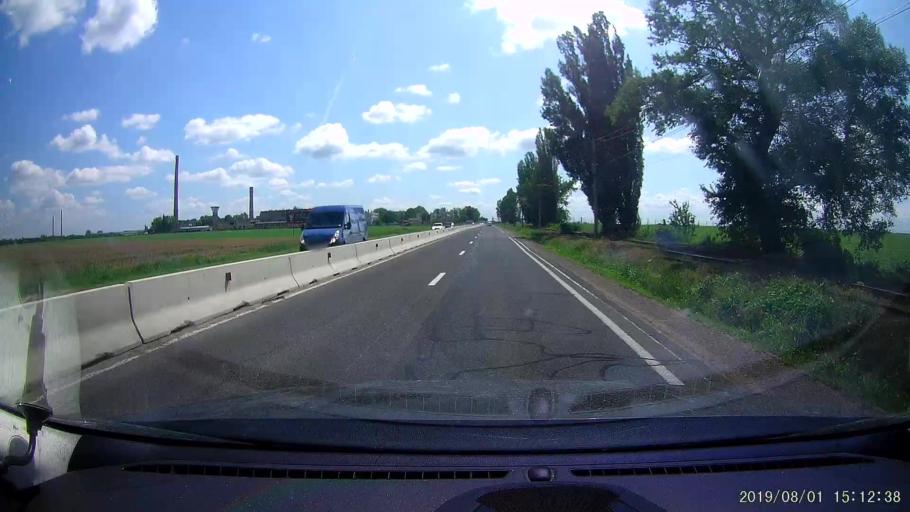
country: RO
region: Braila
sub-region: Comuna Chiscani
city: Lacu Sarat
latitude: 45.2038
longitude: 27.9110
